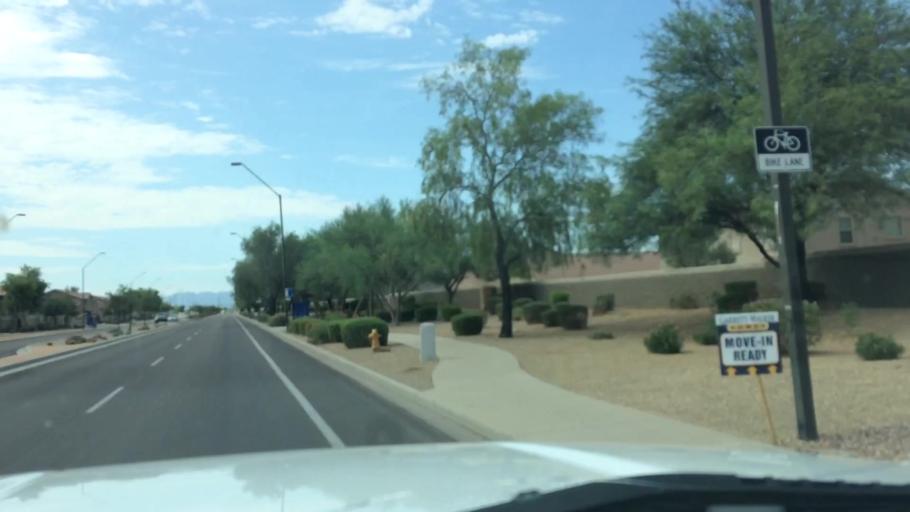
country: US
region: Arizona
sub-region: Maricopa County
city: Peoria
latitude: 33.5736
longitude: -112.2378
